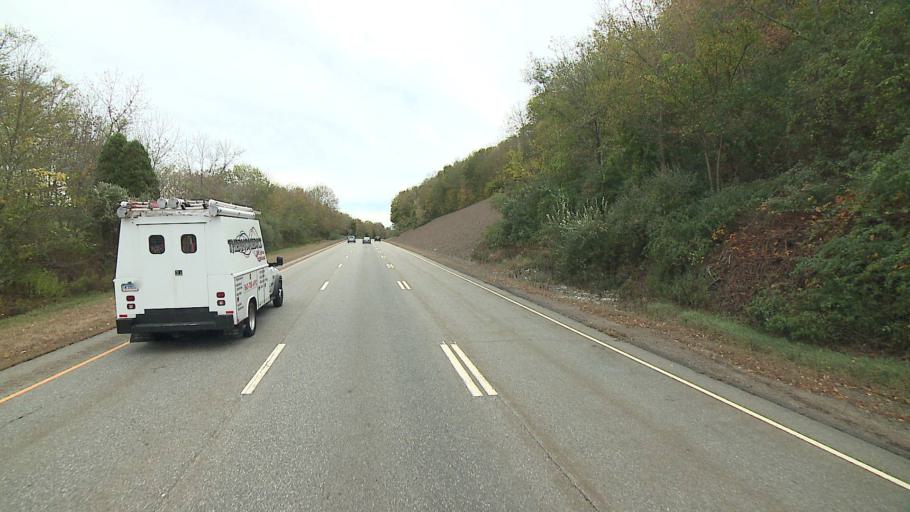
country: US
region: Connecticut
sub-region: Middlesex County
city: East Haddam
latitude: 41.4220
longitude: -72.4980
